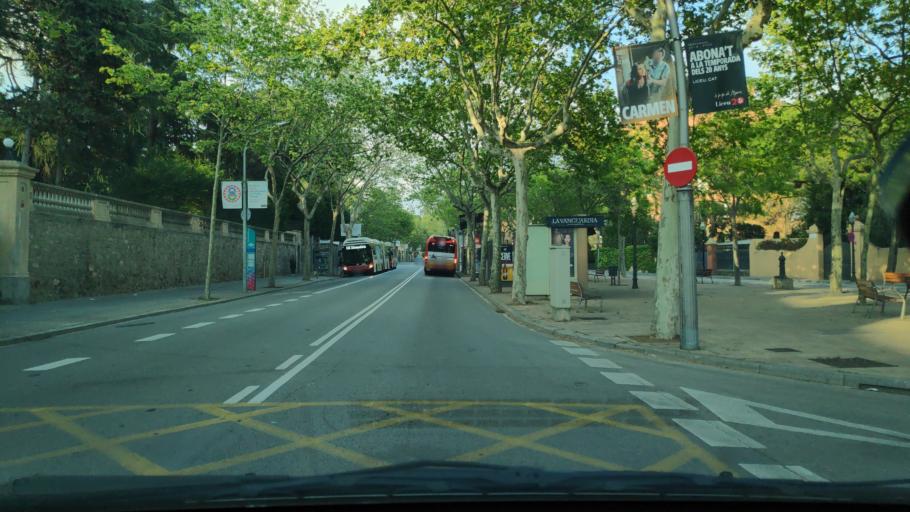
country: ES
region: Catalonia
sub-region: Provincia de Barcelona
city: les Corts
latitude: 41.3956
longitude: 2.1139
